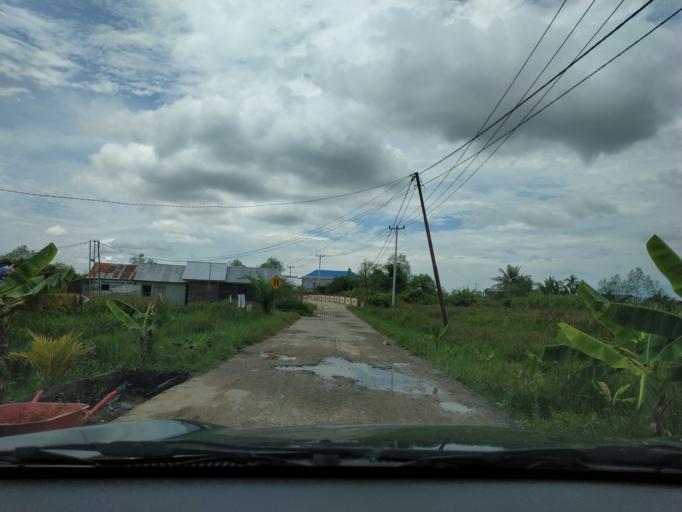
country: ID
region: Riau
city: Tembilahan
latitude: -0.3099
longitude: 103.1792
